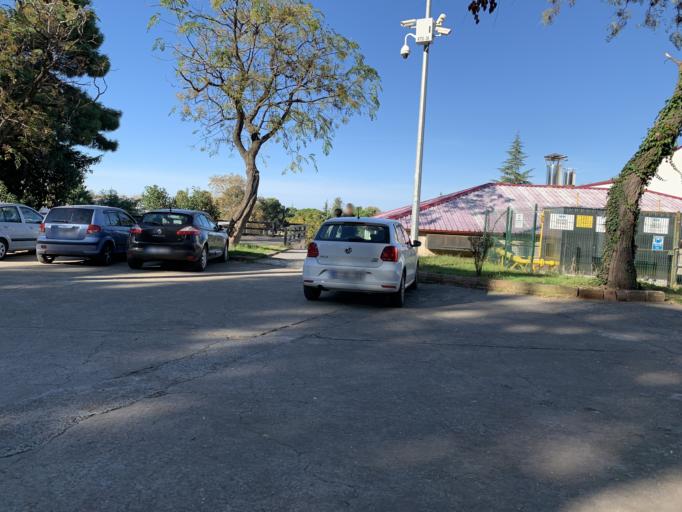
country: TR
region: Trabzon
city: Trabzon
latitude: 40.9959
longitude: 39.7688
